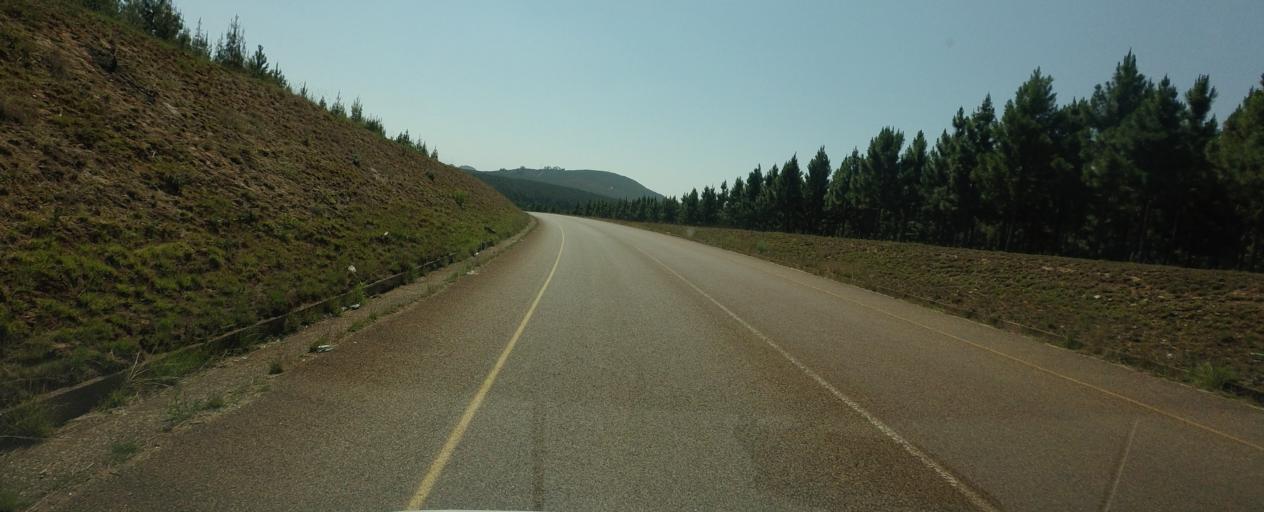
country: ZA
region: Mpumalanga
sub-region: Ehlanzeni District
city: Graksop
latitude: -24.7873
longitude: 30.8684
